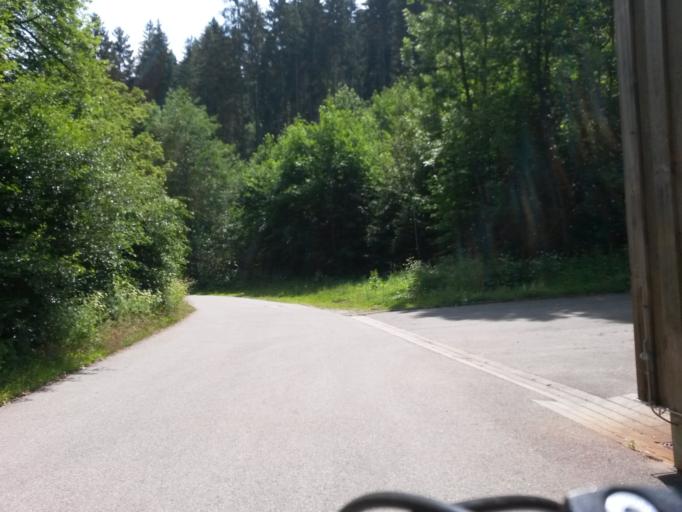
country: DE
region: Baden-Wuerttemberg
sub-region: Karlsruhe Region
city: Wildberg
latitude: 48.6430
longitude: 8.7378
